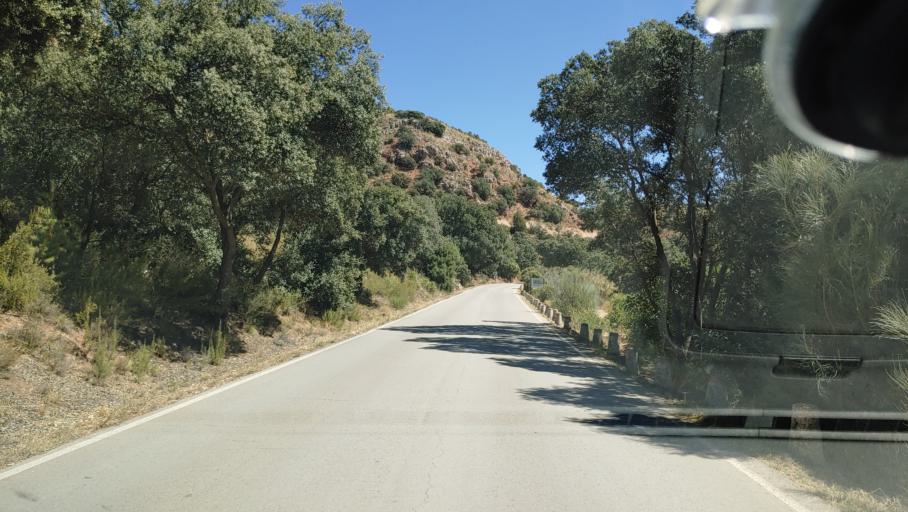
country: ES
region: Castille-La Mancha
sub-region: Provincia de Ciudad Real
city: Ruidera
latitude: 38.9520
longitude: -2.8584
